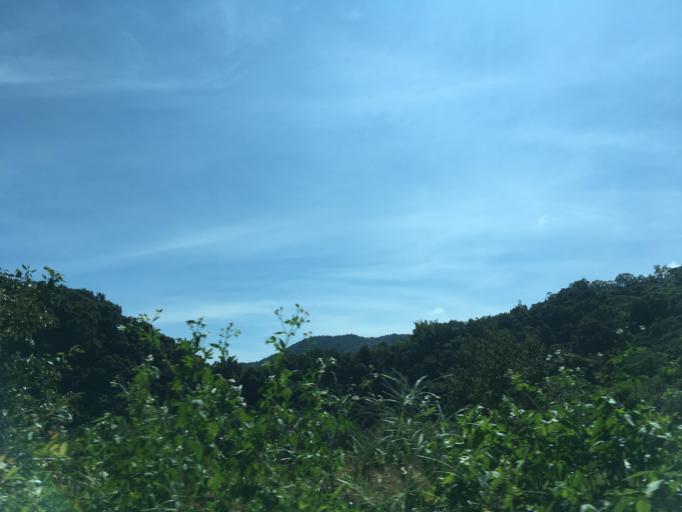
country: TW
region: Taiwan
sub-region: Yilan
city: Yilan
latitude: 24.4193
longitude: 121.7326
